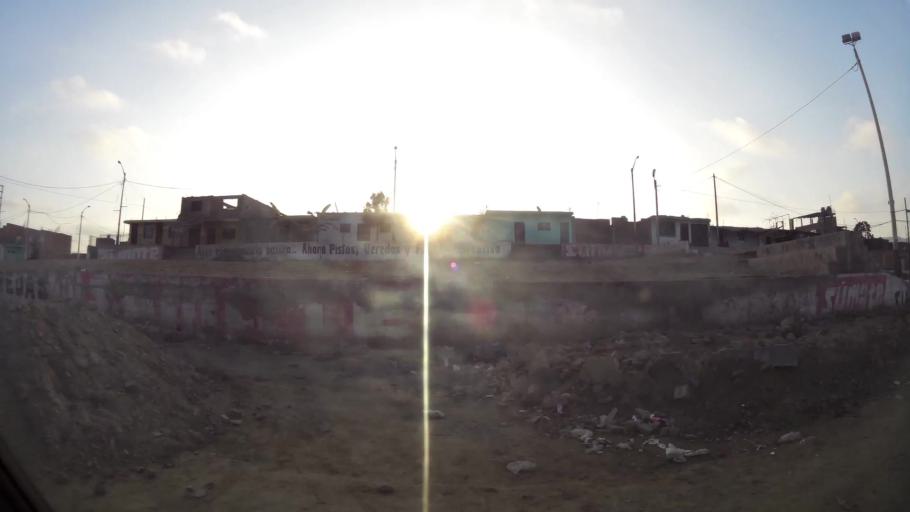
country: PE
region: La Libertad
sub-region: Provincia de Trujillo
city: El Porvenir
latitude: -8.0690
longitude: -78.9968
